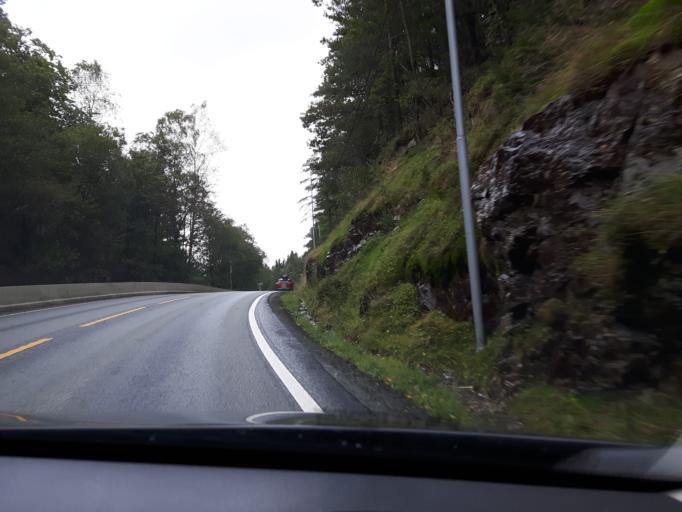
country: NO
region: Vest-Agder
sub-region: Marnardal
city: Helland
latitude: 58.0821
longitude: 7.6152
